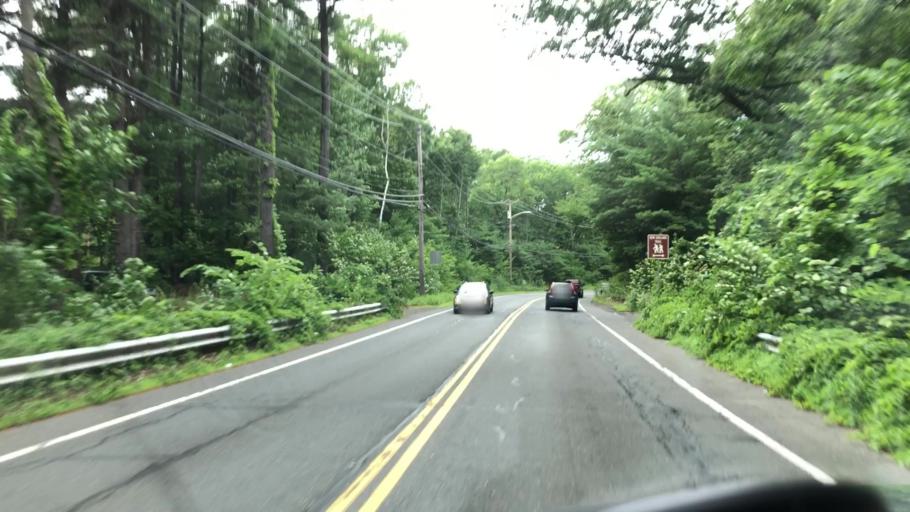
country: US
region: Massachusetts
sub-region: Hampden County
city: Holyoke
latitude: 42.2246
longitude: -72.6452
